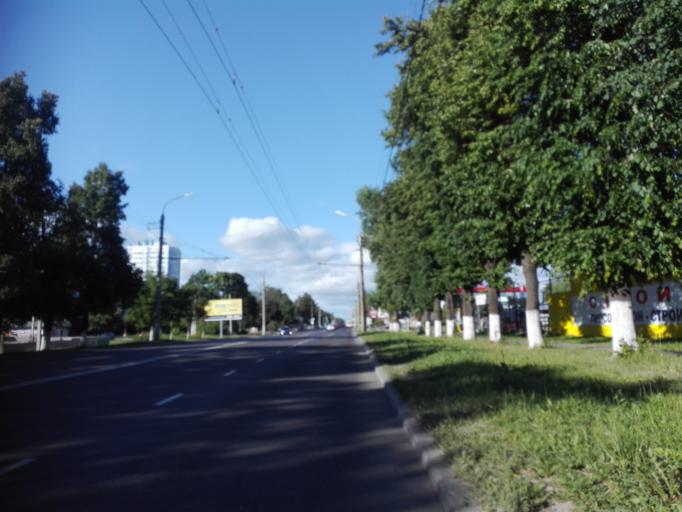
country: RU
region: Orjol
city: Orel
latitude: 52.9974
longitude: 36.1342
